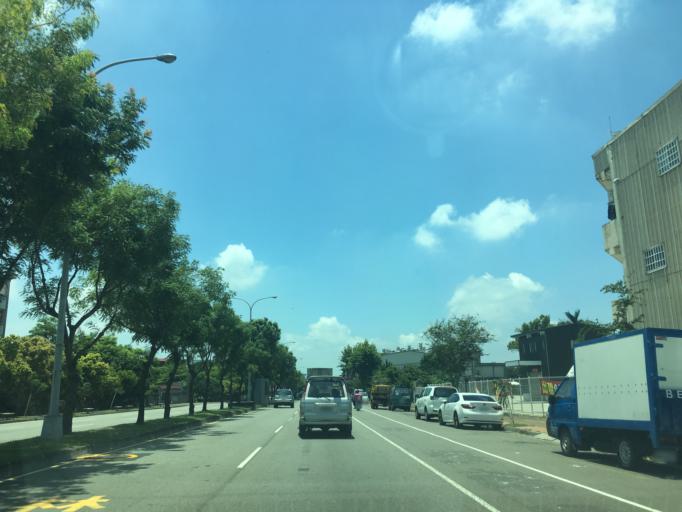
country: TW
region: Taiwan
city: Fengyuan
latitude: 24.2414
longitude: 120.7031
